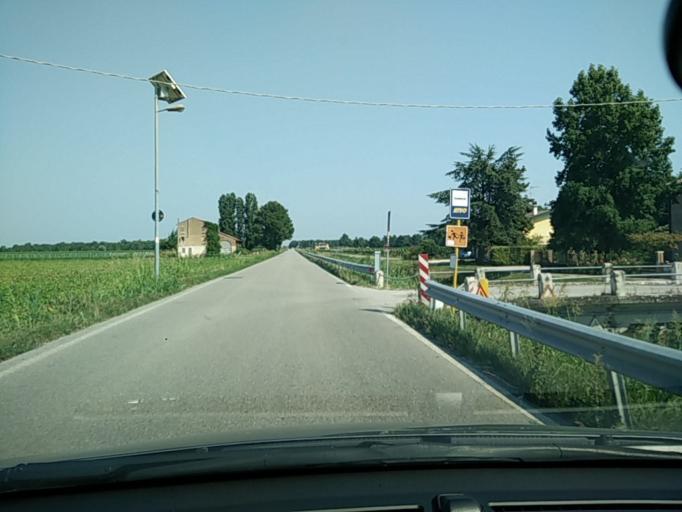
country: IT
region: Veneto
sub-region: Provincia di Venezia
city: Passarella
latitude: 45.6188
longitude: 12.6331
